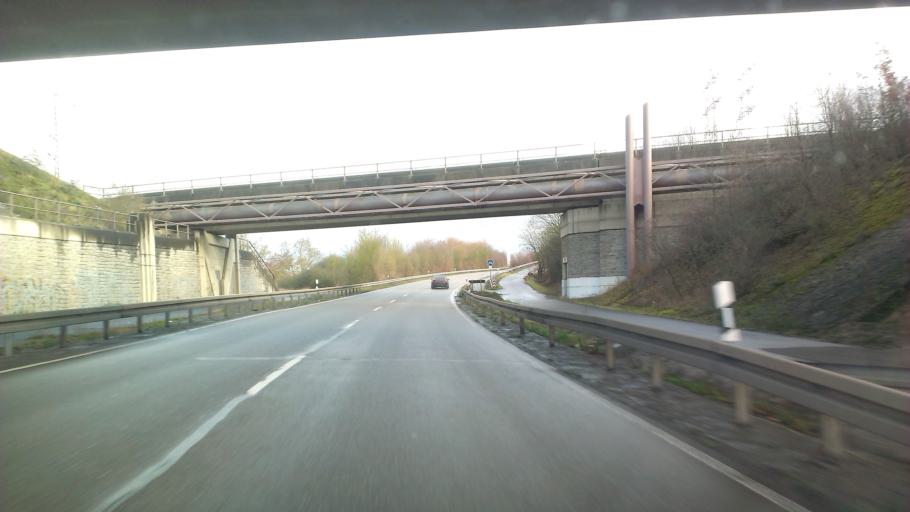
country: DE
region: Baden-Wuerttemberg
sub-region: Karlsruhe Region
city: Ubstadt-Weiher
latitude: 49.1492
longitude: 8.6174
